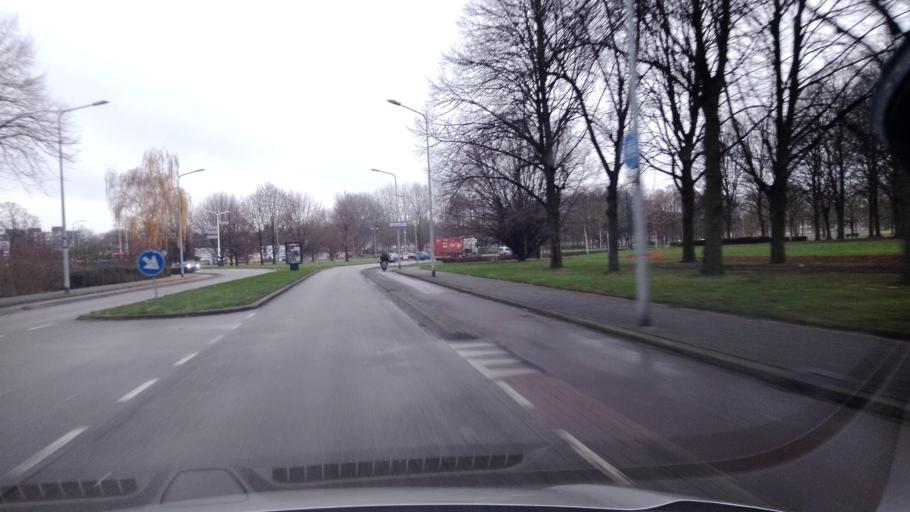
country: NL
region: Limburg
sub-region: Gemeente Maastricht
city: Maastricht
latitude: 50.8549
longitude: 5.6657
